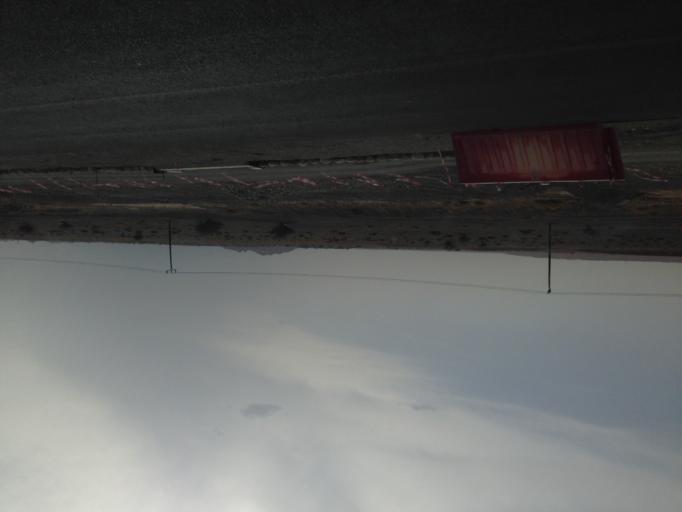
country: OM
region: Ash Sharqiyah
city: Al Qabil
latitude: 22.5474
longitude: 58.7212
